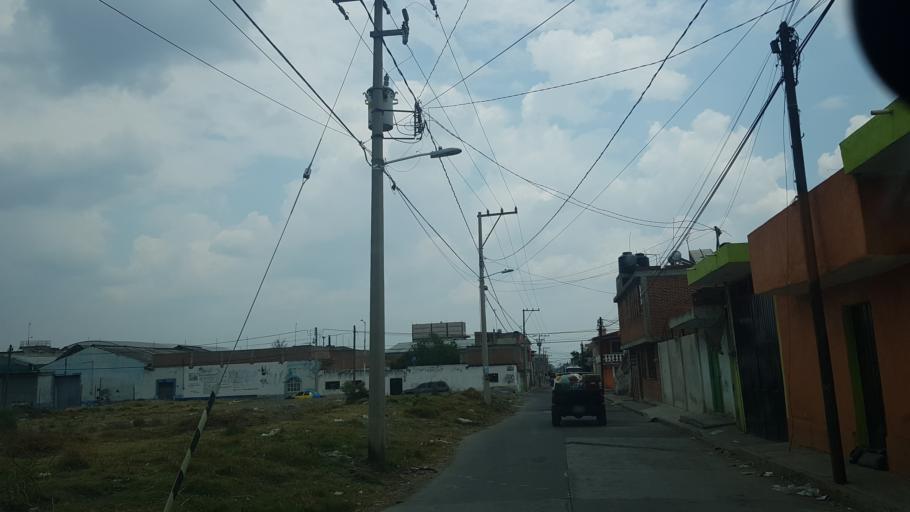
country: MX
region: Puebla
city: Huejotzingo
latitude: 19.1648
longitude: -98.4106
